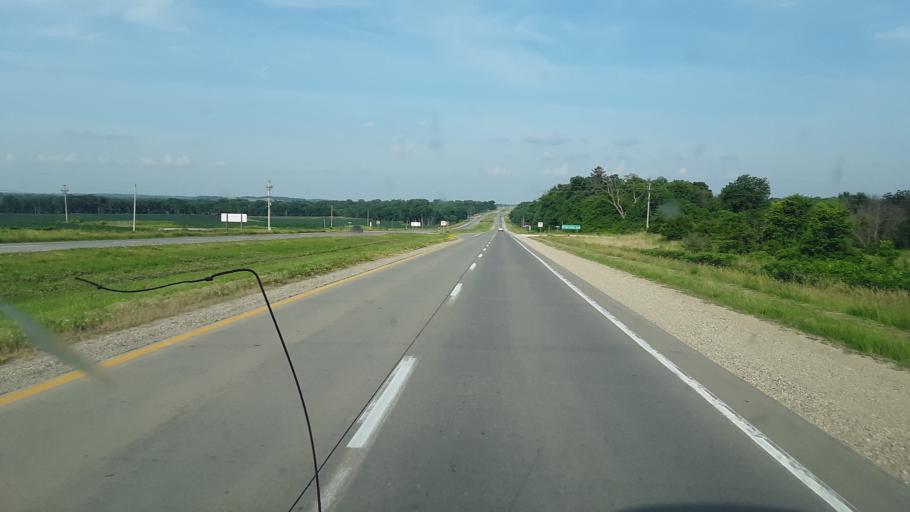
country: US
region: Iowa
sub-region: Marshall County
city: Marshalltown
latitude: 42.0068
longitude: -92.8643
